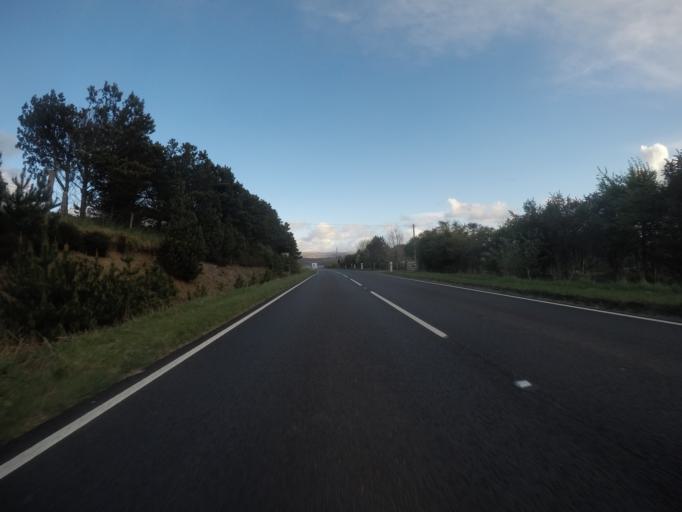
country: GB
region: Scotland
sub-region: Highland
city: Portree
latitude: 57.4936
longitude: -6.3200
